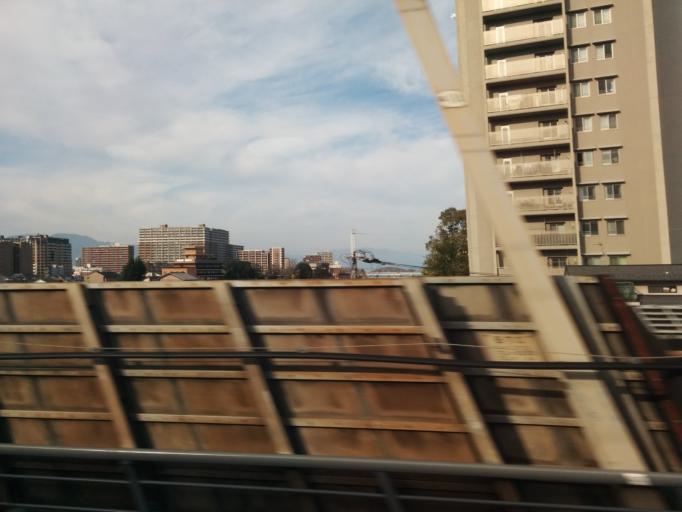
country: JP
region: Shiga Prefecture
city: Otsu-shi
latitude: 34.9697
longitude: 135.9070
